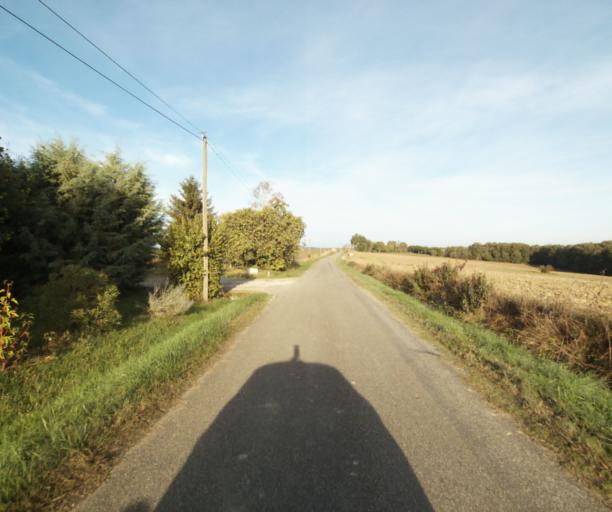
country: FR
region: Midi-Pyrenees
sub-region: Departement de la Haute-Garonne
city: Villemur-sur-Tarn
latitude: 43.9085
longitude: 1.4827
